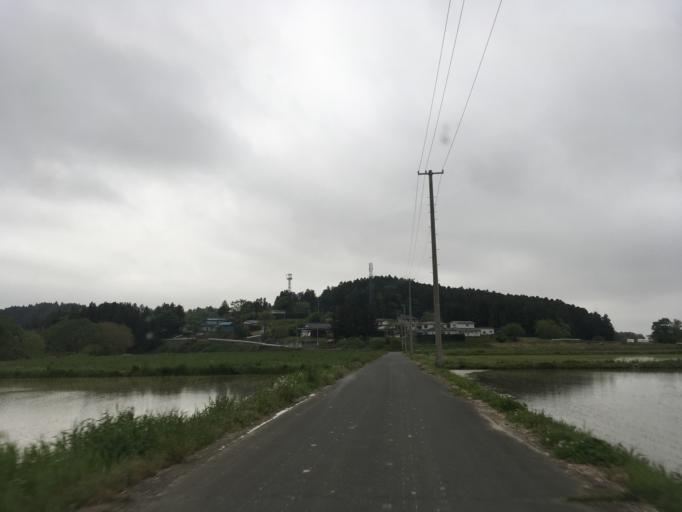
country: JP
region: Miyagi
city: Wakuya
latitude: 38.7118
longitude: 141.2855
